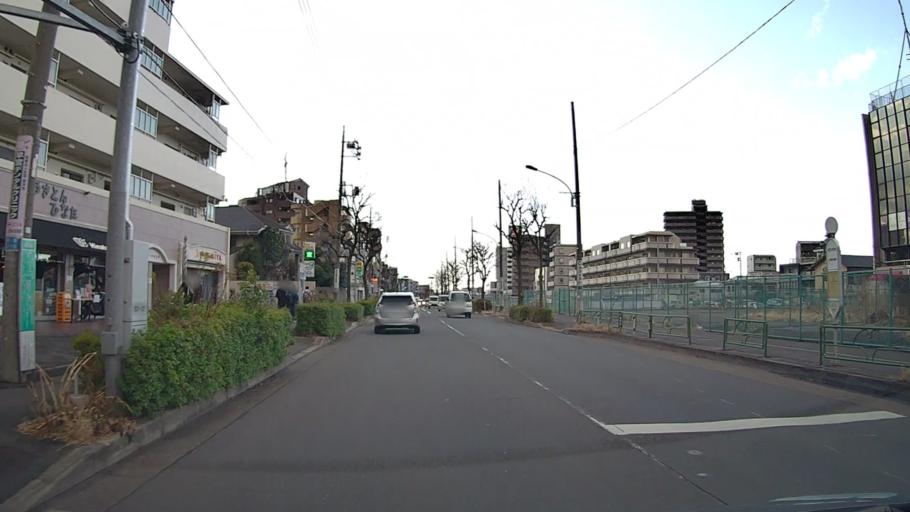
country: JP
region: Saitama
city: Wako
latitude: 35.7564
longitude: 139.6563
